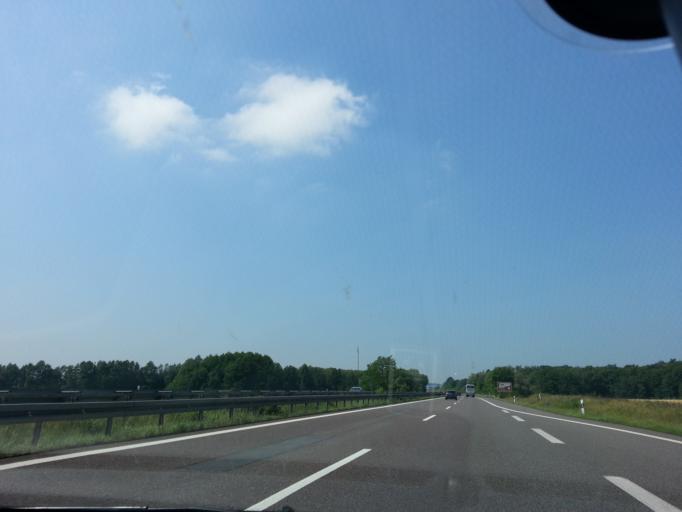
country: DE
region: Brandenburg
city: Gerdshagen
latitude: 53.1993
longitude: 12.2723
